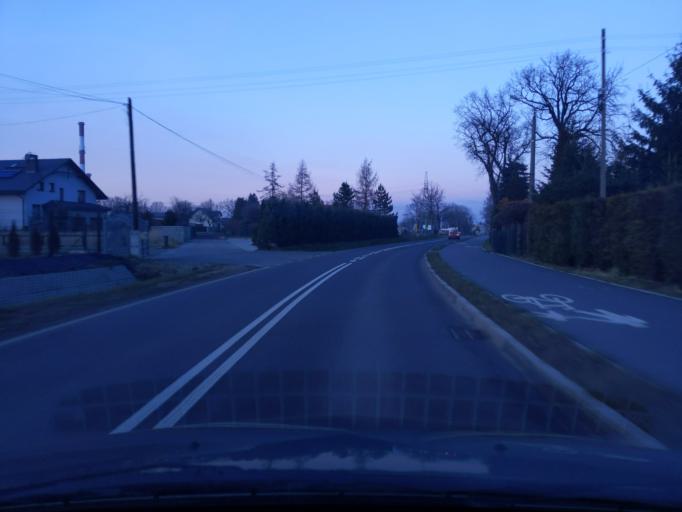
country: PL
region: Silesian Voivodeship
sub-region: Powiat pszczynski
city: Pszczyna
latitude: 49.9575
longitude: 18.9331
